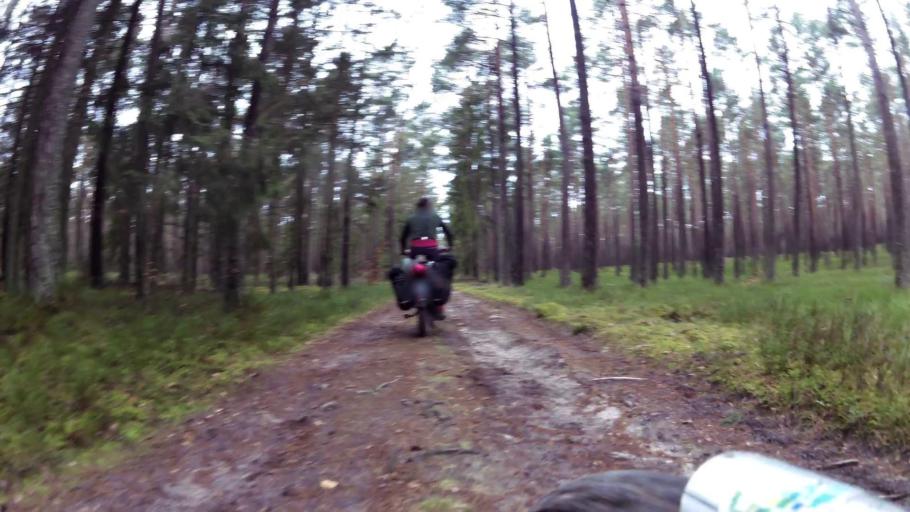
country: PL
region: Pomeranian Voivodeship
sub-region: Powiat bytowski
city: Kolczyglowy
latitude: 54.2388
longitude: 17.2596
